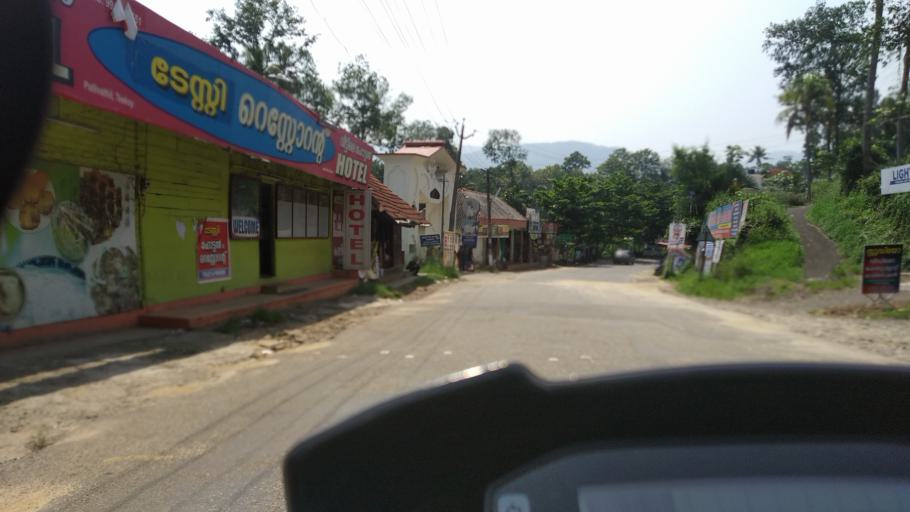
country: IN
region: Kerala
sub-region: Kottayam
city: Erattupetta
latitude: 9.6996
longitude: 76.8086
